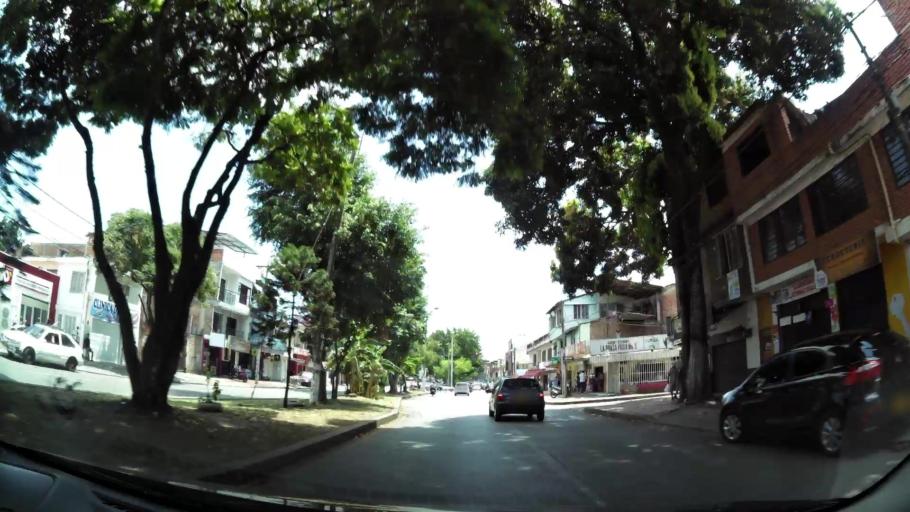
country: CO
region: Valle del Cauca
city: Cali
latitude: 3.4489
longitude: -76.5042
